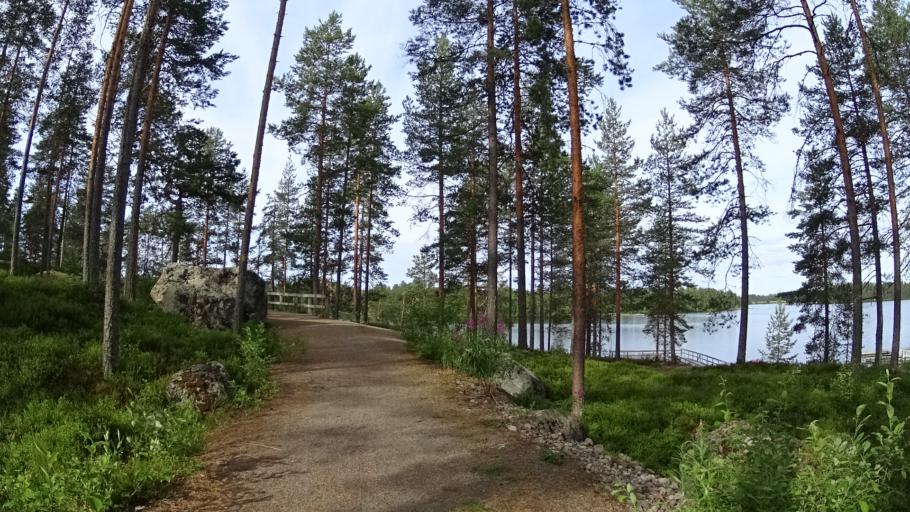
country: FI
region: Southern Ostrobothnia
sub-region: Kuusiokunnat
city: AEhtaeri
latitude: 62.5361
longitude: 24.1797
